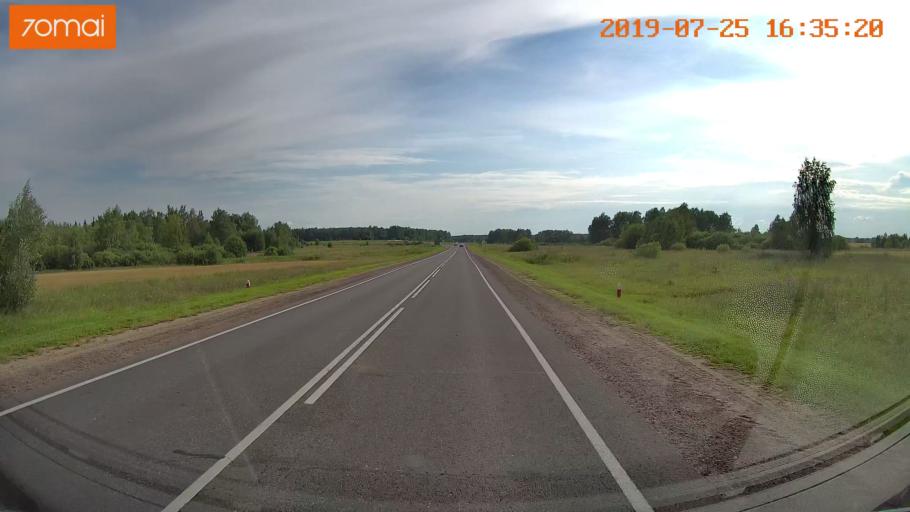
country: RU
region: Ivanovo
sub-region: Privolzhskiy Rayon
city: Ples
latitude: 57.4066
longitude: 41.4222
